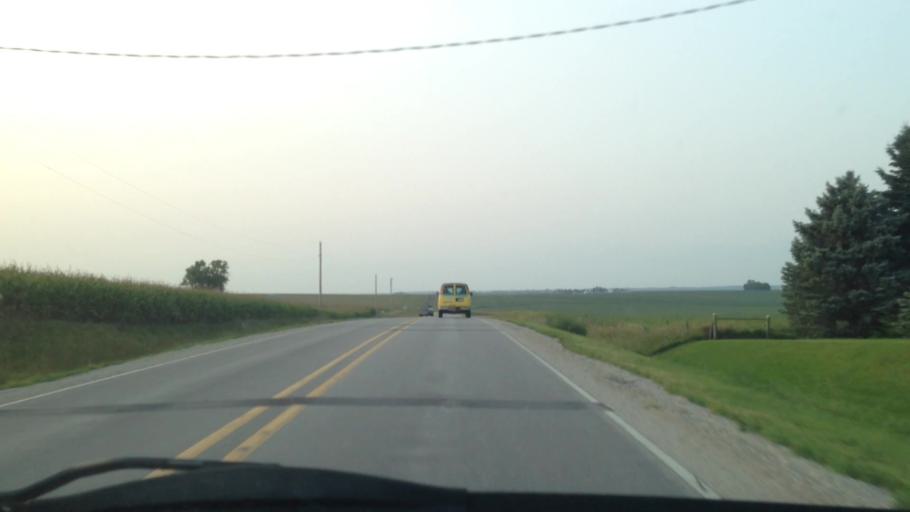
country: US
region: Iowa
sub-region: Benton County
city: Atkins
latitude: 42.0223
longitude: -91.8739
